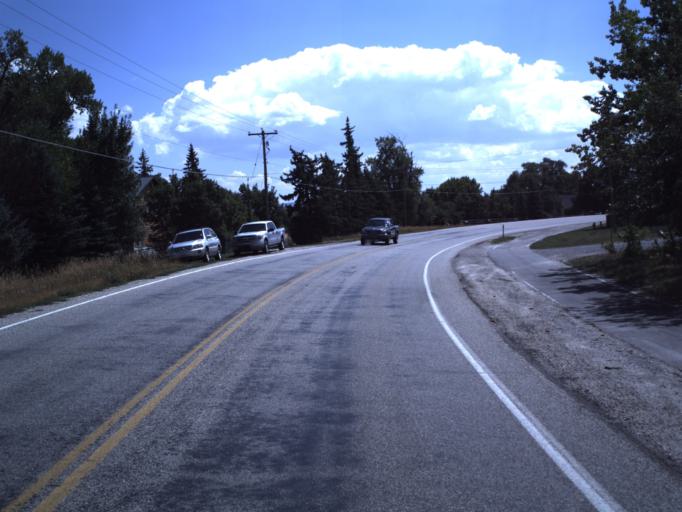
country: US
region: Idaho
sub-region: Bear Lake County
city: Paris
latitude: 41.9533
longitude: -111.3941
